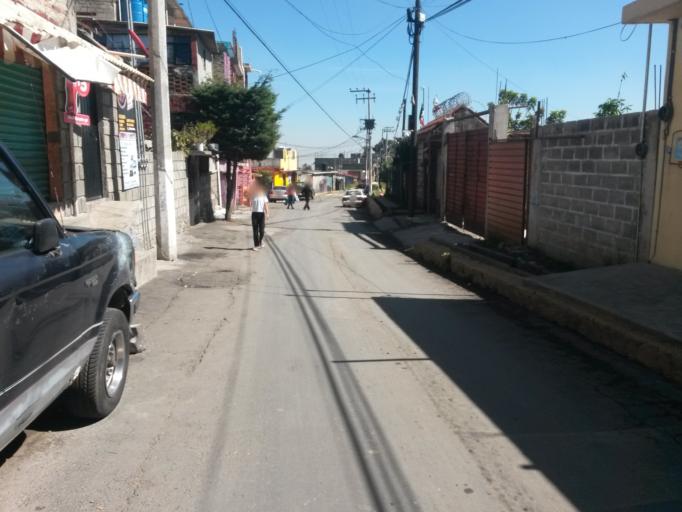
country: MX
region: Mexico City
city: Magdalena Contreras
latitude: 19.2961
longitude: -99.2522
